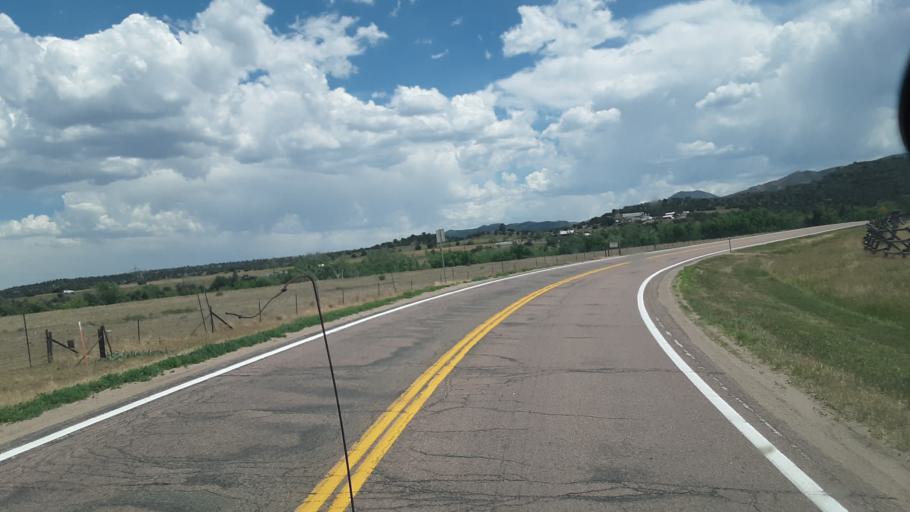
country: US
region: Colorado
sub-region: Fremont County
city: Florence
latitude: 38.2429
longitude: -105.0856
